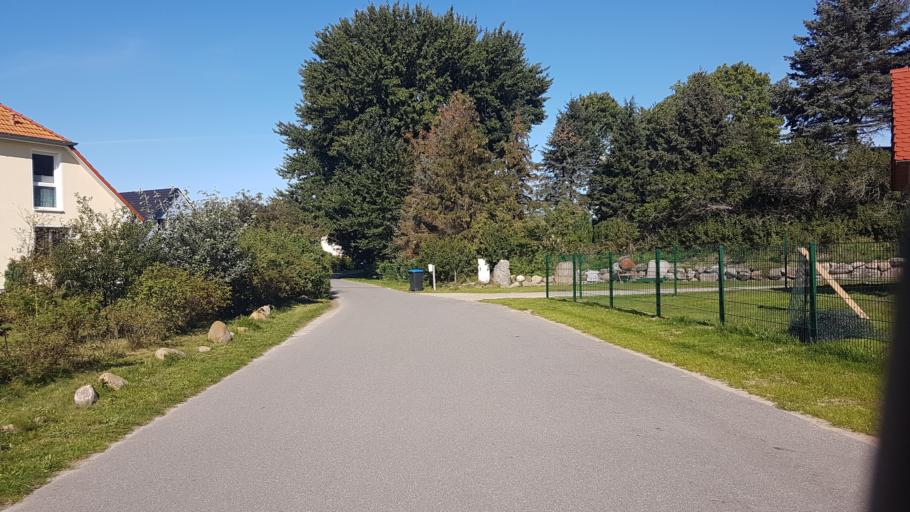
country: DE
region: Mecklenburg-Vorpommern
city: Glowe
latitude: 54.5654
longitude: 13.4754
